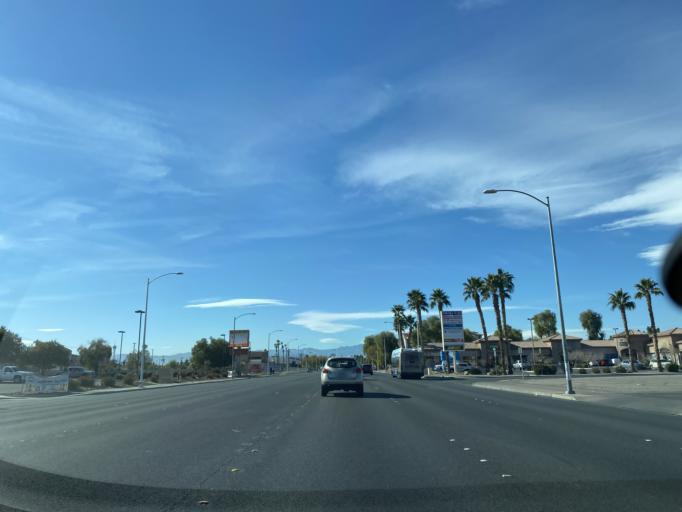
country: US
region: Nevada
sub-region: Clark County
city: Sunrise Manor
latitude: 36.1735
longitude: -115.0820
